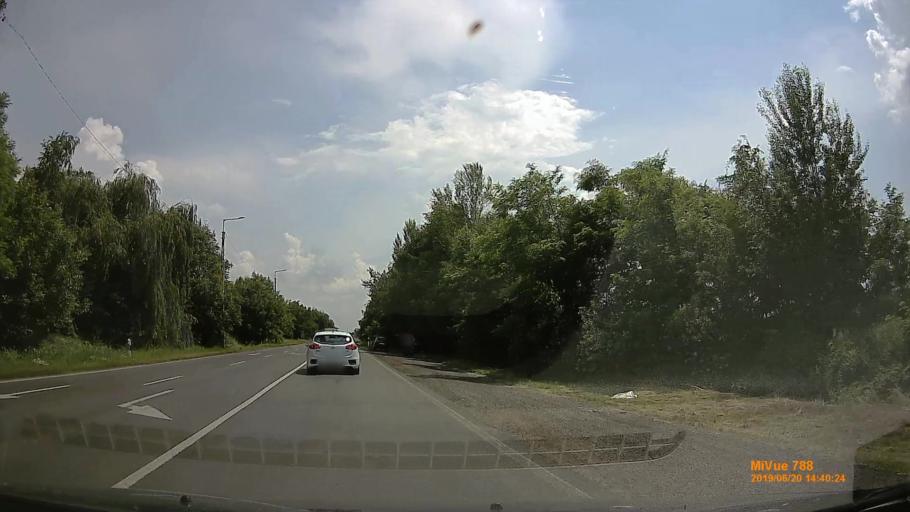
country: HU
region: Baranya
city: Pecs
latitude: 46.0818
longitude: 18.2772
